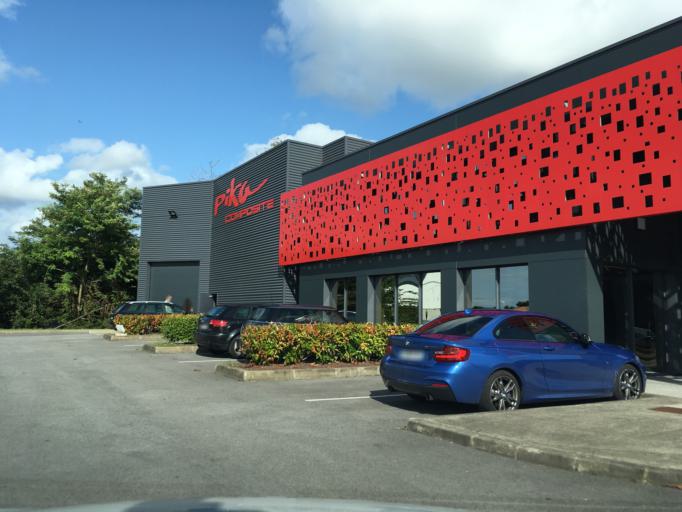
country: FR
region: Aquitaine
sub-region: Departement des Pyrenees-Atlantiques
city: Bayonne
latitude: 43.4664
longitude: -1.4910
